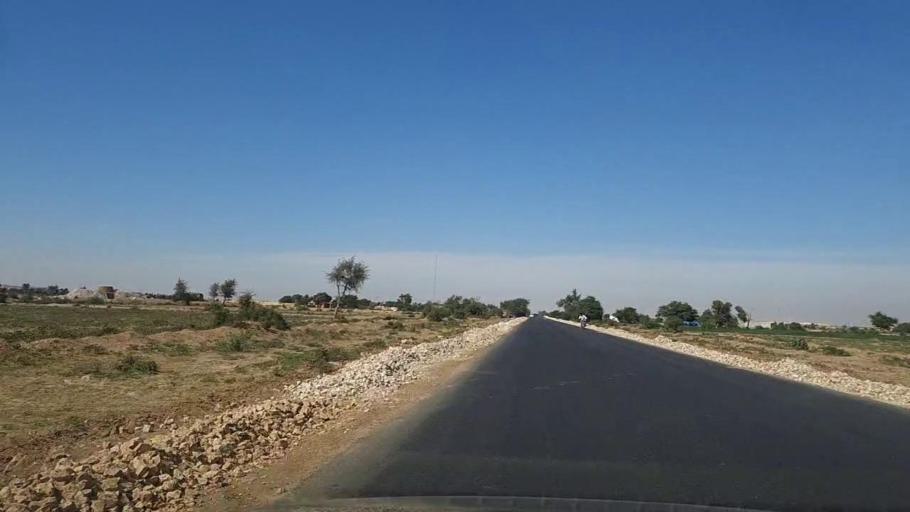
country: PK
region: Sindh
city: Kotri
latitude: 25.2823
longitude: 68.2111
